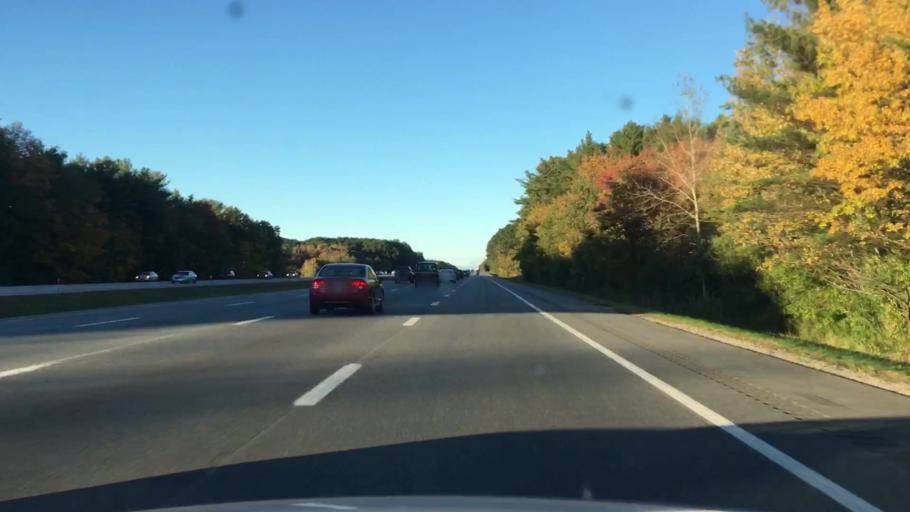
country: US
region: New Hampshire
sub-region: Rockingham County
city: North Hampton
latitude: 42.9974
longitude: -70.8460
